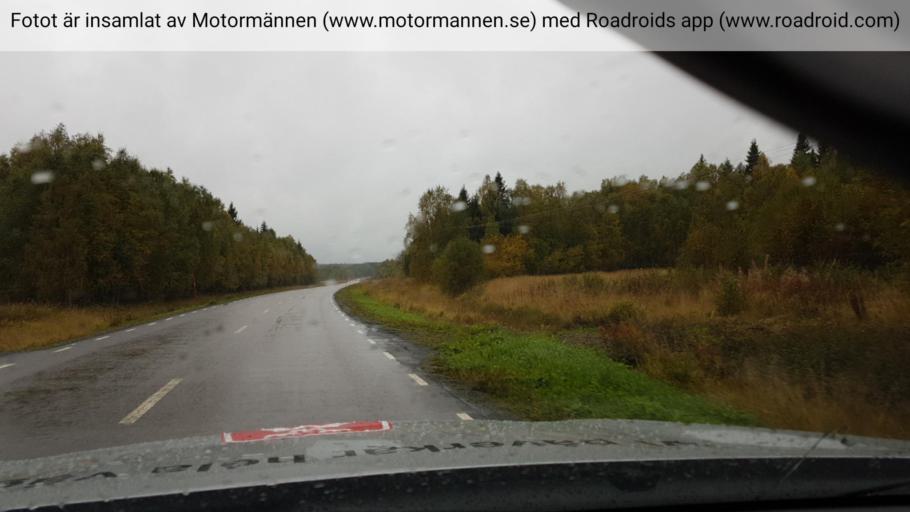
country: SE
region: Norrbotten
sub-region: Lulea Kommun
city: Sodra Sunderbyn
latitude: 65.8266
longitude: 21.9359
